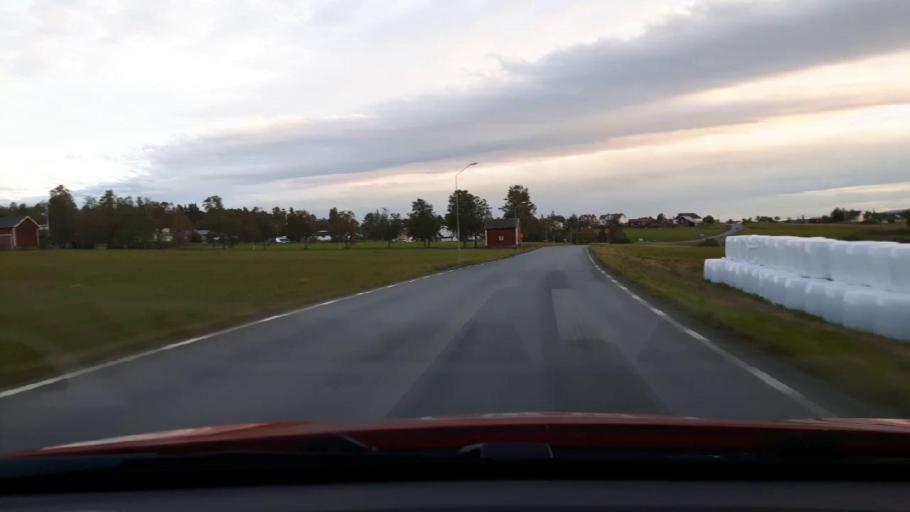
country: SE
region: Jaemtland
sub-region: OEstersunds Kommun
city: Ostersund
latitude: 63.1107
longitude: 14.4354
